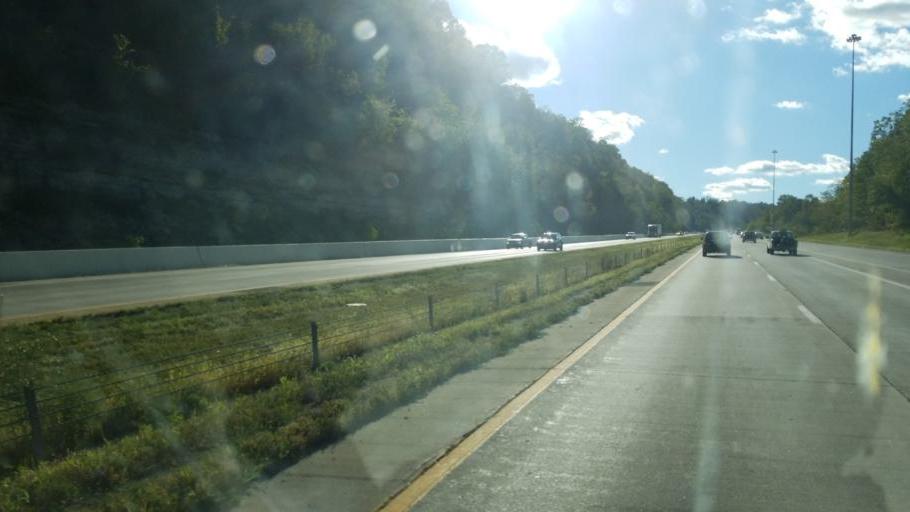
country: US
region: Ohio
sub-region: Belmont County
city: Bridgeport
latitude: 40.0481
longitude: -80.7414
